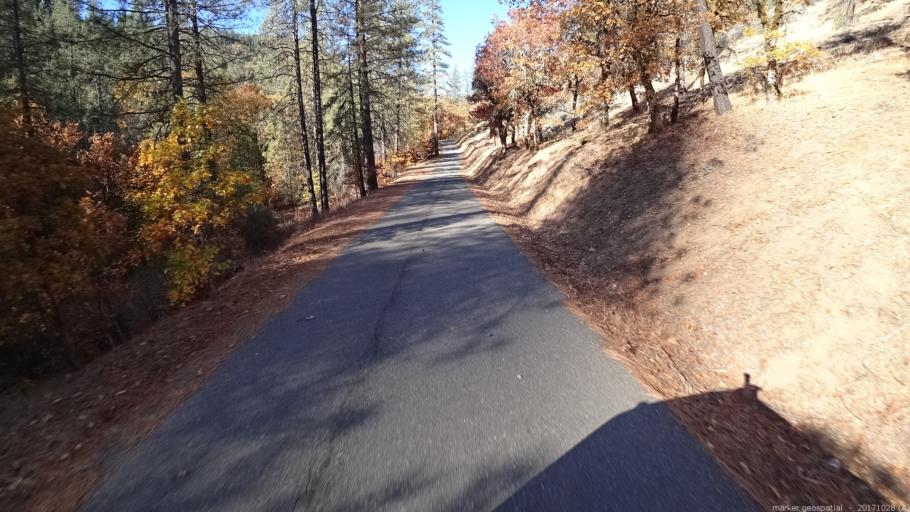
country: US
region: California
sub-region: Shasta County
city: Shasta
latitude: 40.7565
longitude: -122.5897
